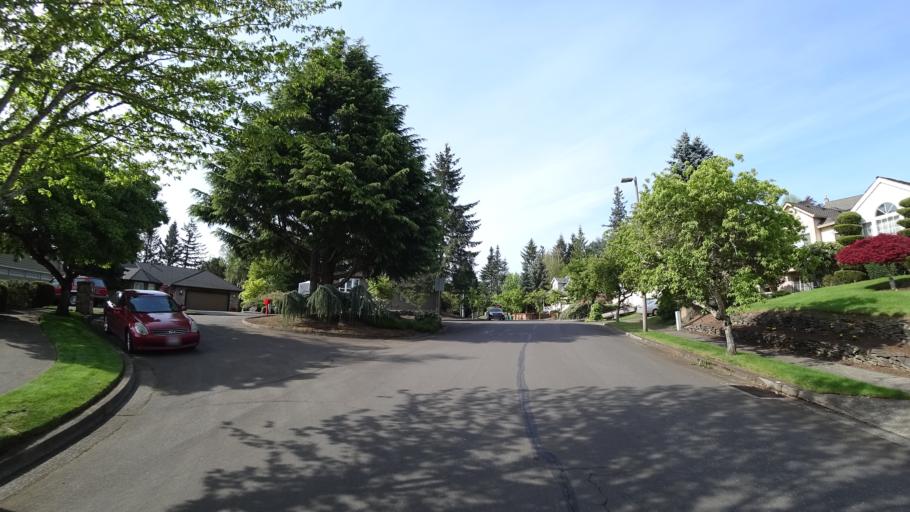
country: US
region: Oregon
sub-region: Washington County
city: Aloha
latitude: 45.4483
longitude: -122.8422
